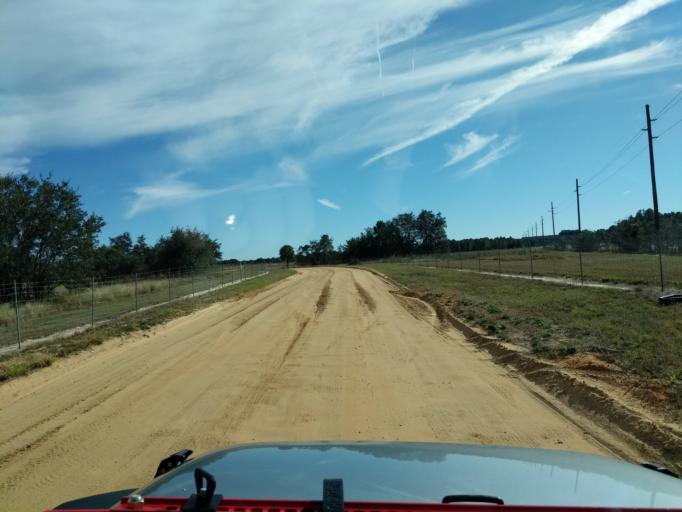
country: US
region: Florida
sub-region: Lake County
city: Clermont
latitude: 28.4826
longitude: -81.7145
